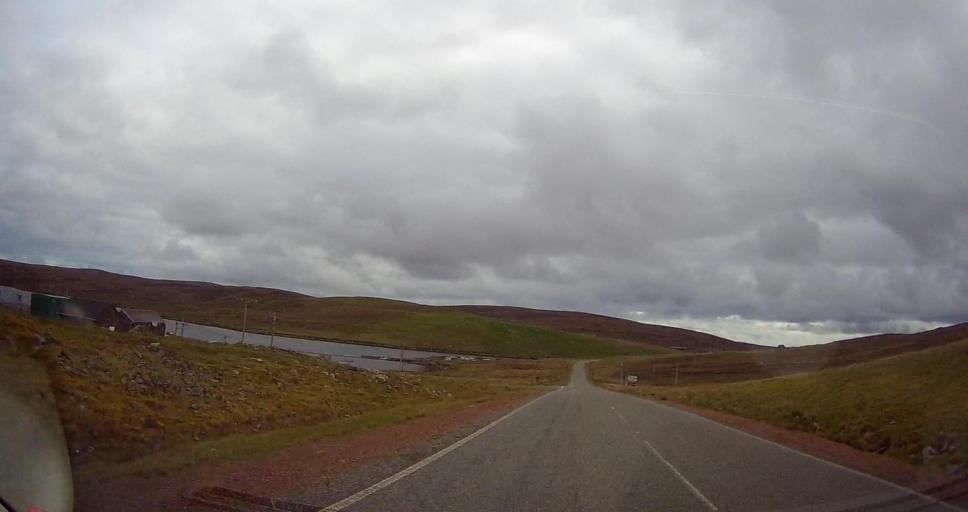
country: GB
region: Scotland
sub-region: Shetland Islands
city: Shetland
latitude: 60.6024
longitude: -1.1232
